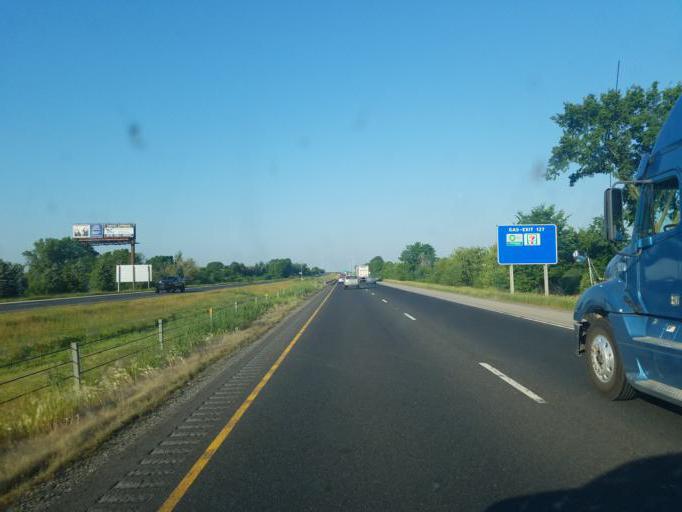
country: US
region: Illinois
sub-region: Will County
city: Rockdale
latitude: 41.5034
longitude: -88.1537
